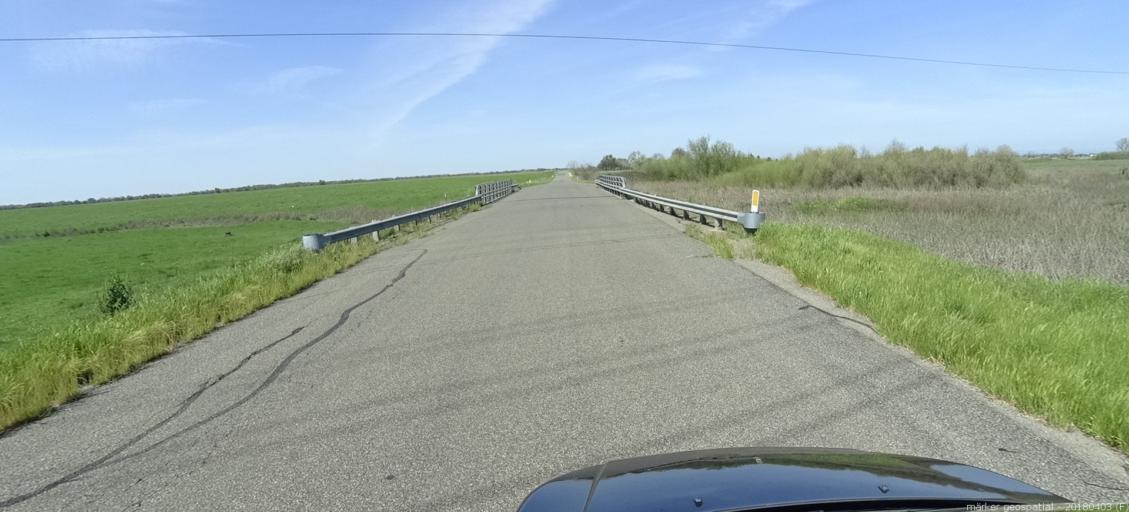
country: US
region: California
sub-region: Sacramento County
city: Wilton
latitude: 38.3511
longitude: -121.2976
